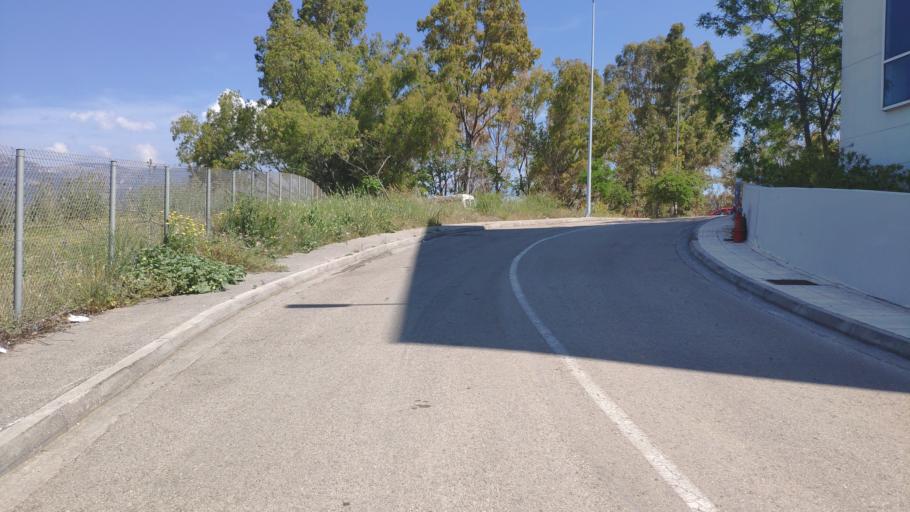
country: GR
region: Attica
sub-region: Nomarchia Athinas
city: Metamorfosi
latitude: 38.0797
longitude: 23.7693
